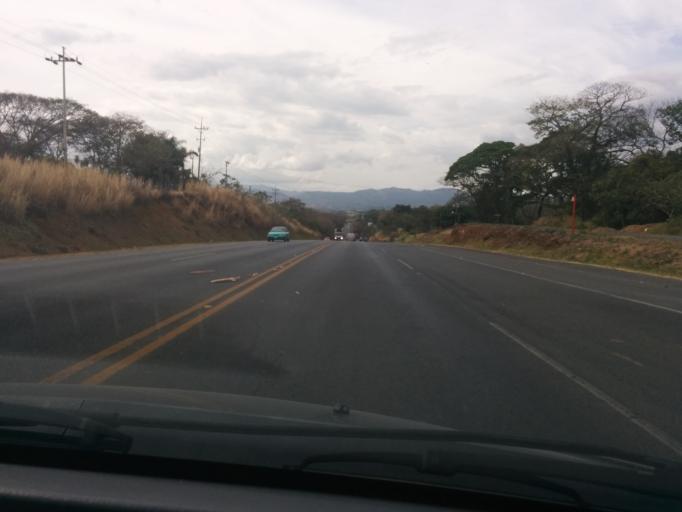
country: CR
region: Alajuela
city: Carrillos
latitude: 10.0010
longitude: -84.2828
